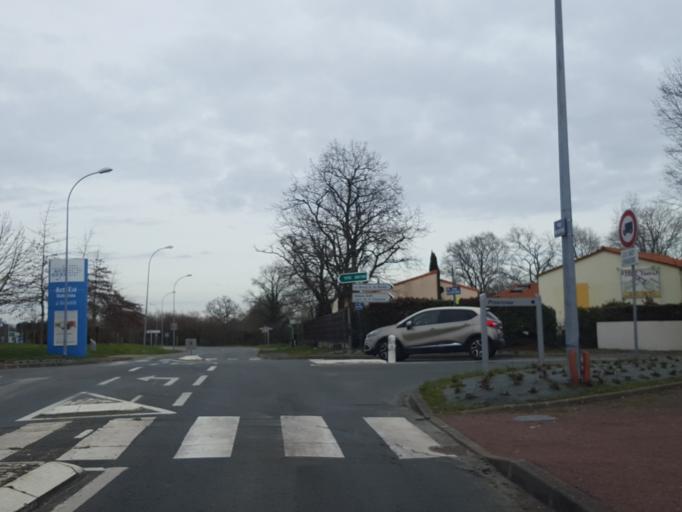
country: FR
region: Pays de la Loire
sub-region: Departement de la Vendee
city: La Roche-sur-Yon
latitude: 46.6748
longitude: -1.4004
